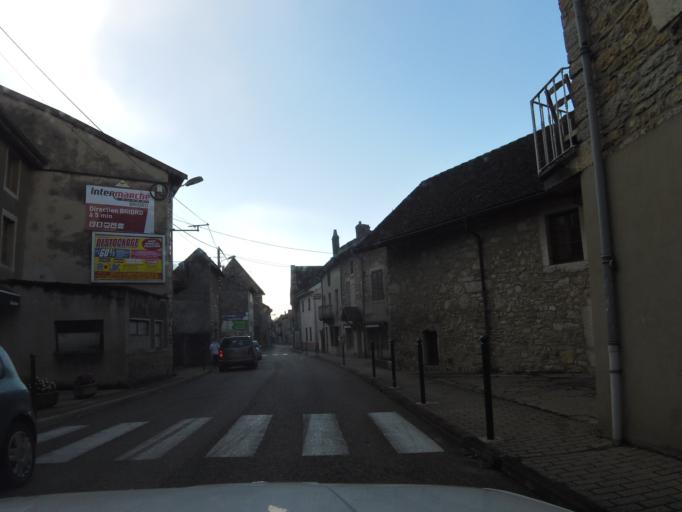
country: FR
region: Rhone-Alpes
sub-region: Departement de l'Isere
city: Bouvesse-Quirieu
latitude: 45.8081
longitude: 5.4534
